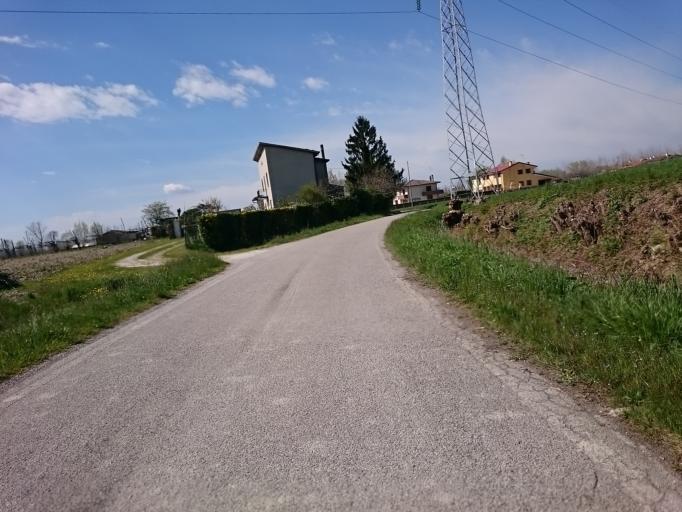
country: IT
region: Veneto
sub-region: Provincia di Padova
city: Polverara
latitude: 45.3078
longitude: 11.9731
